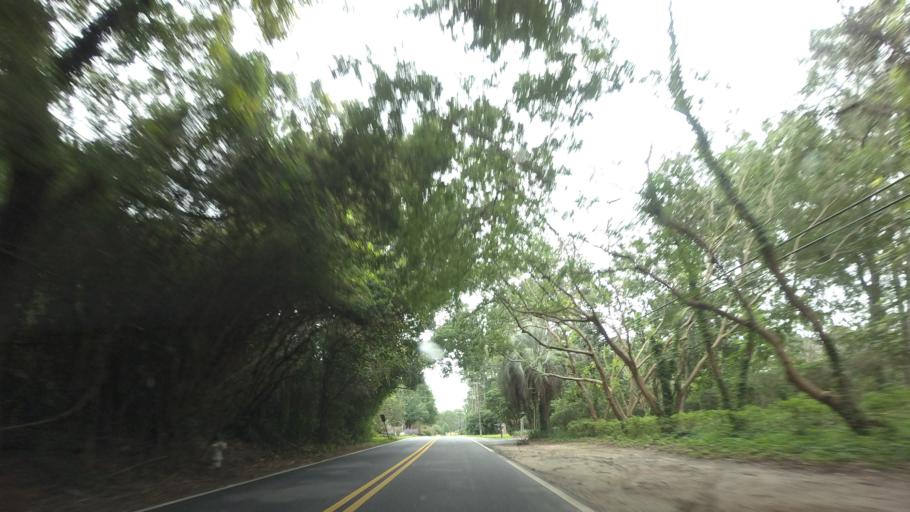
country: US
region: Georgia
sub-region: Lowndes County
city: Remerton
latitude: 30.8851
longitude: -83.3083
